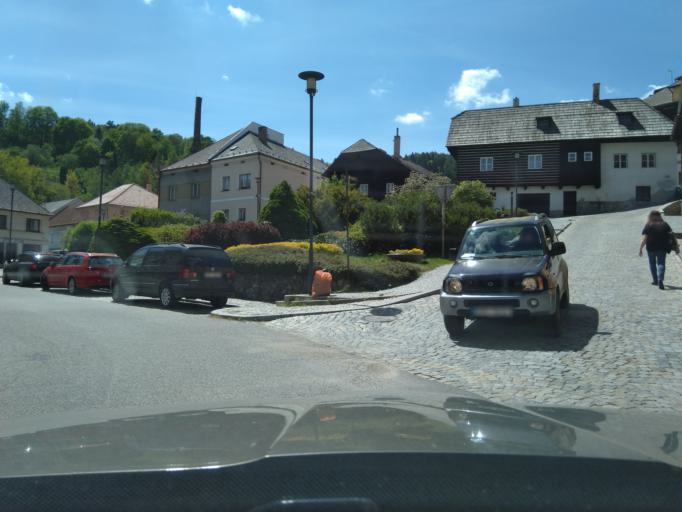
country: CZ
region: Jihocesky
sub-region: Okres Prachatice
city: Vimperk
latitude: 49.0525
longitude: 13.7761
